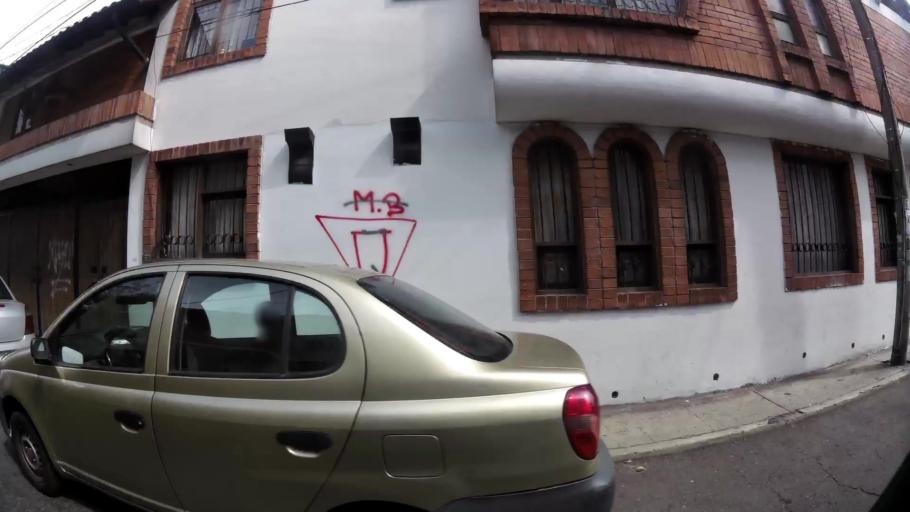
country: EC
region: Pichincha
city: Quito
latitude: -0.2152
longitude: -78.4878
